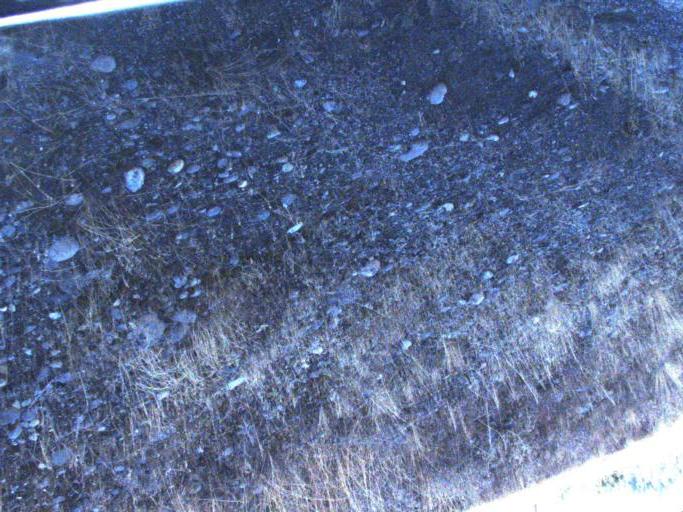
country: US
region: Washington
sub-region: Ferry County
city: Republic
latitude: 48.7676
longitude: -118.6465
